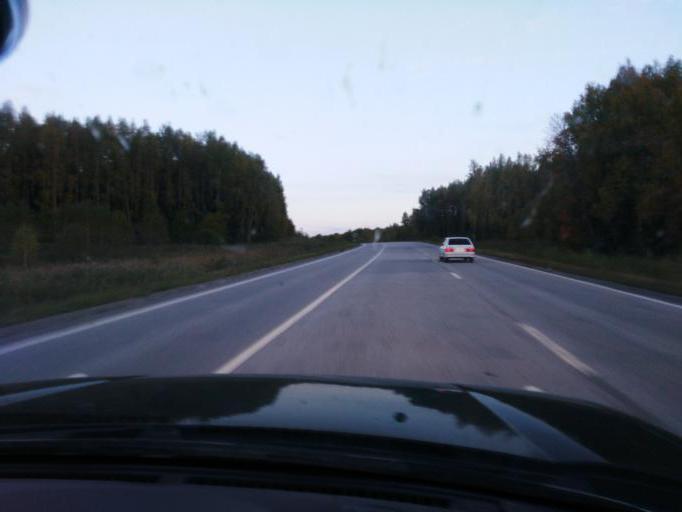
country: RU
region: Perm
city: Verkhnechusovskiye Gorodki
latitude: 58.2868
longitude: 56.8975
